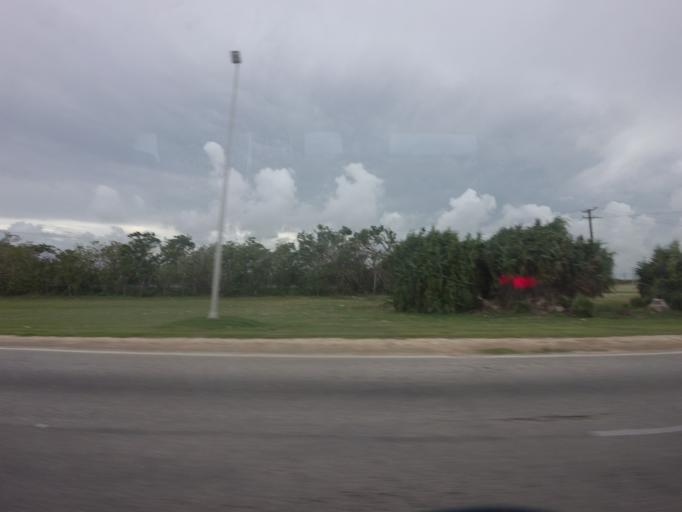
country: CU
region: Matanzas
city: Varadero
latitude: 23.1285
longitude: -81.3145
